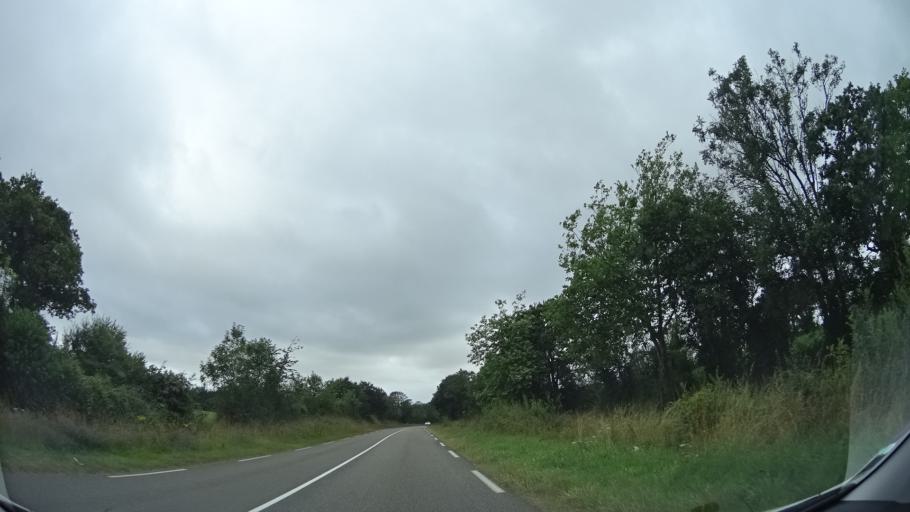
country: FR
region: Lower Normandy
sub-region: Departement de la Manche
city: Portbail
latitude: 49.3193
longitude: -1.6269
